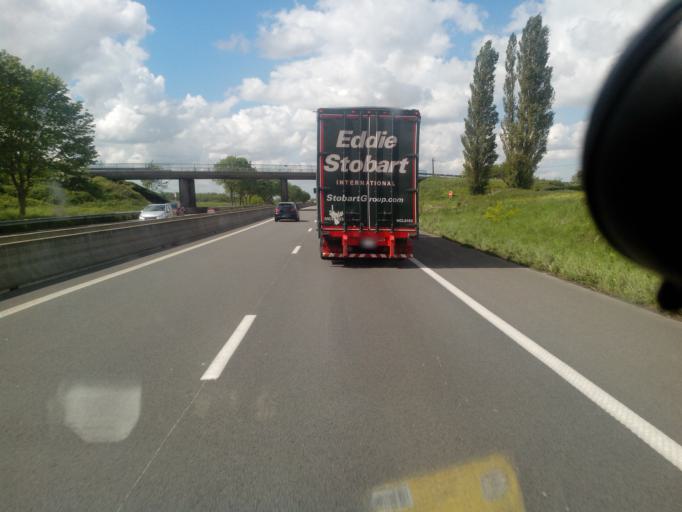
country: FR
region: Nord-Pas-de-Calais
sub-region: Departement du Nord
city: Godewaersvelde
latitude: 50.7780
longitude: 2.6291
